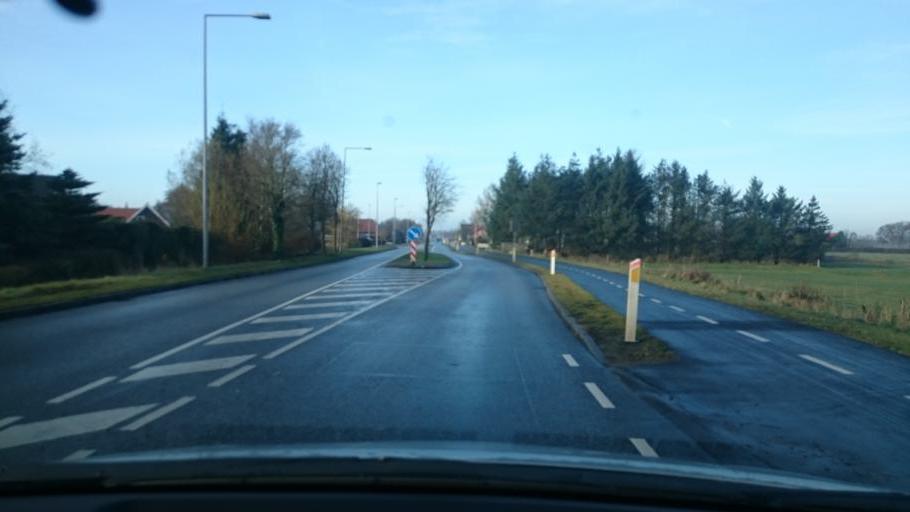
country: DK
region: South Denmark
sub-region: Esbjerg Kommune
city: Ribe
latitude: 55.3169
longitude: 8.7771
